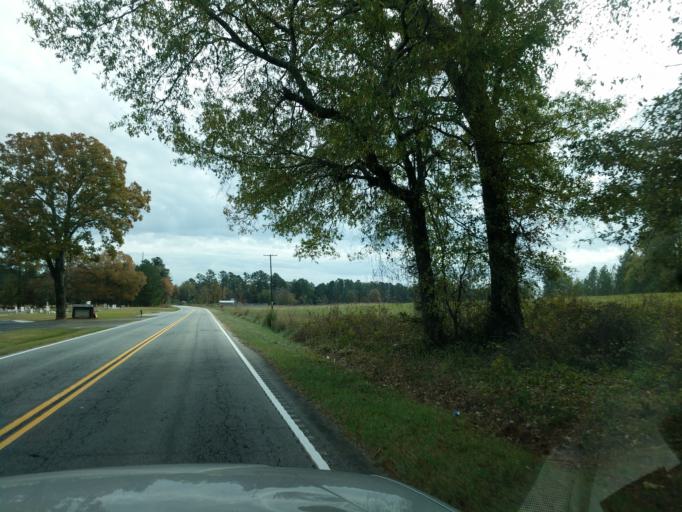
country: US
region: South Carolina
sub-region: Greenwood County
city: Ninety Six
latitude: 34.1937
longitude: -81.8790
